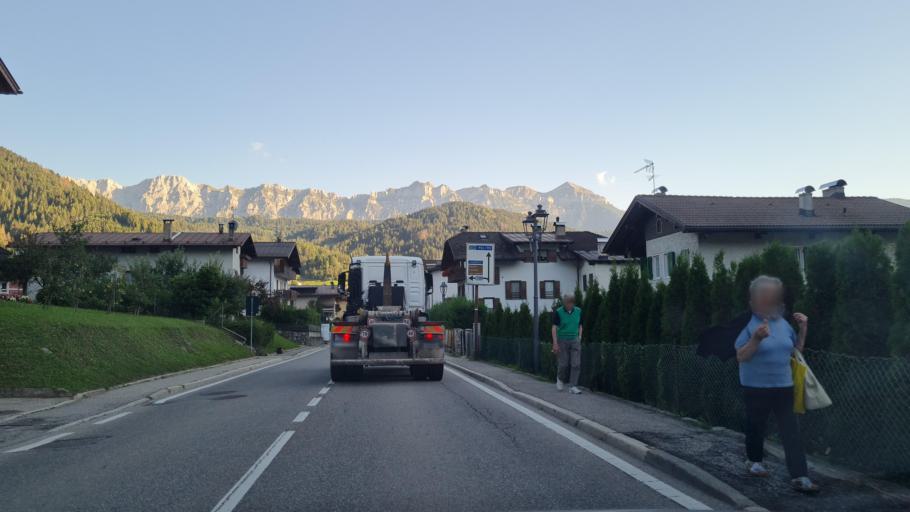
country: IT
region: Trentino-Alto Adige
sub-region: Provincia di Trento
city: Fiera di Primiero
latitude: 46.1810
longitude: 11.8321
